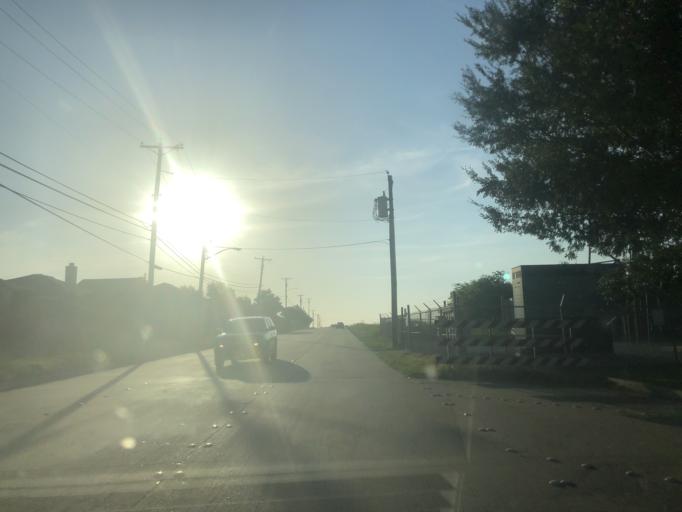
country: US
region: Texas
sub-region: Tarrant County
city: White Settlement
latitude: 32.7317
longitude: -97.5076
